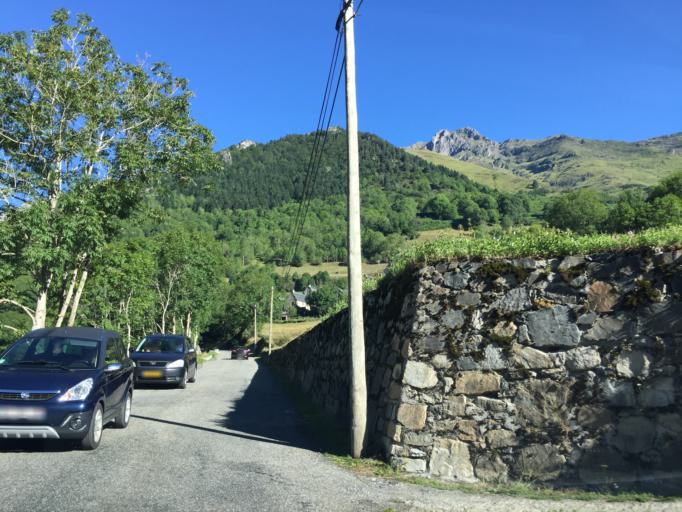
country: FR
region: Midi-Pyrenees
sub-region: Departement des Hautes-Pyrenees
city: Saint-Lary-Soulan
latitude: 42.8488
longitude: 0.2968
